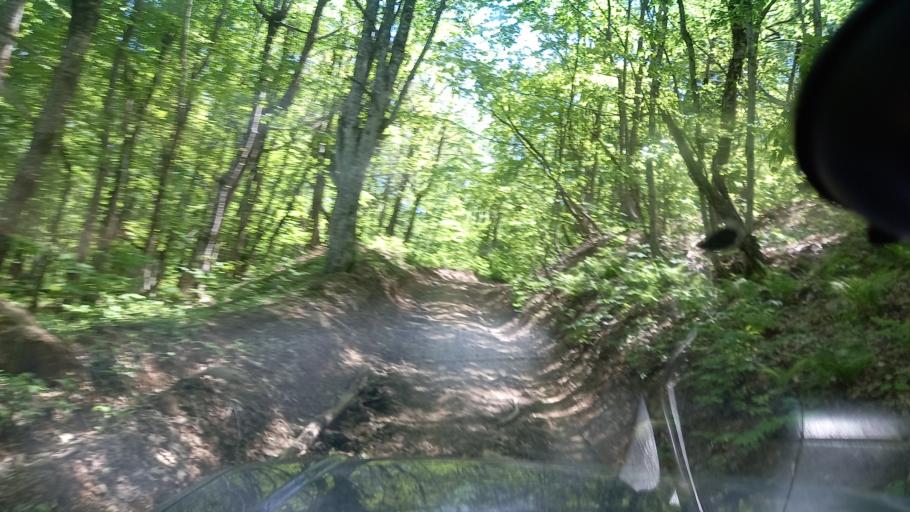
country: RU
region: Krasnodarskiy
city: Tuapse
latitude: 44.2609
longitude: 39.2831
